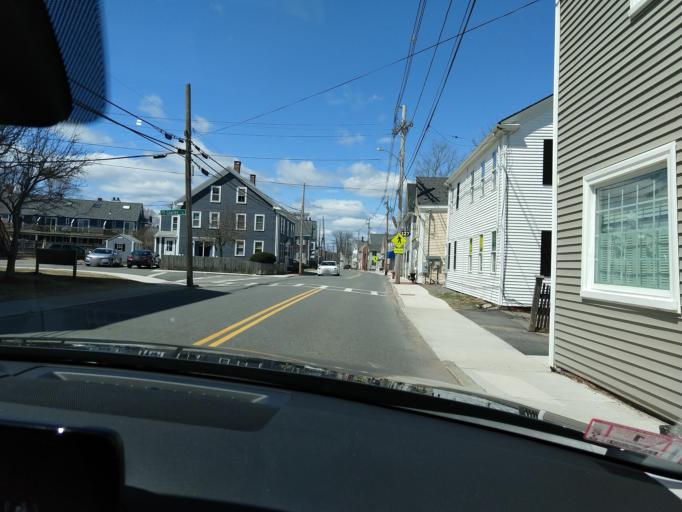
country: US
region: Massachusetts
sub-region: Essex County
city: Newburyport
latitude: 42.8089
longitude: -70.8622
